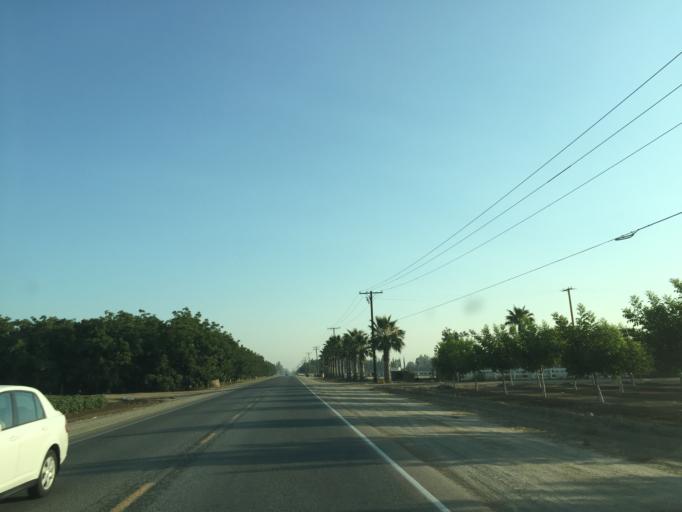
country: US
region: California
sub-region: Tulare County
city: Visalia
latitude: 36.3739
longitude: -119.2788
